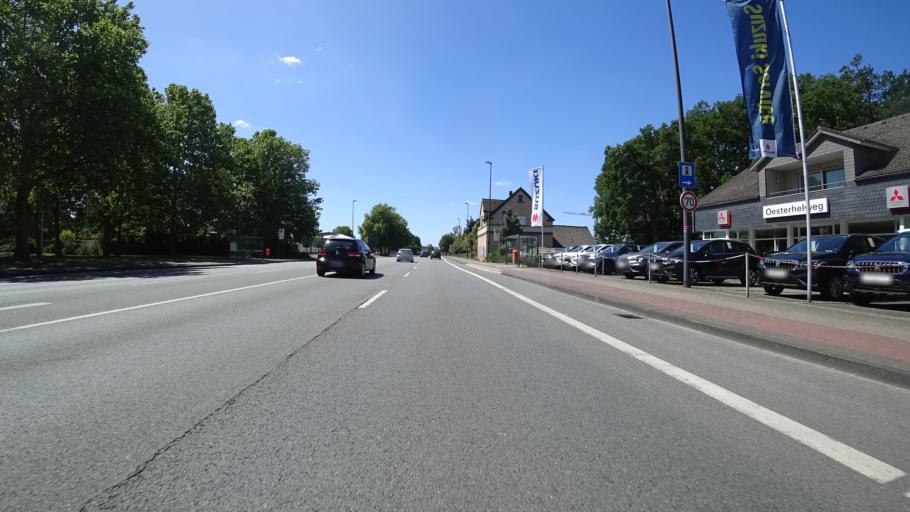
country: DE
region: North Rhine-Westphalia
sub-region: Regierungsbezirk Detmold
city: Guetersloh
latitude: 51.9204
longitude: 8.3977
